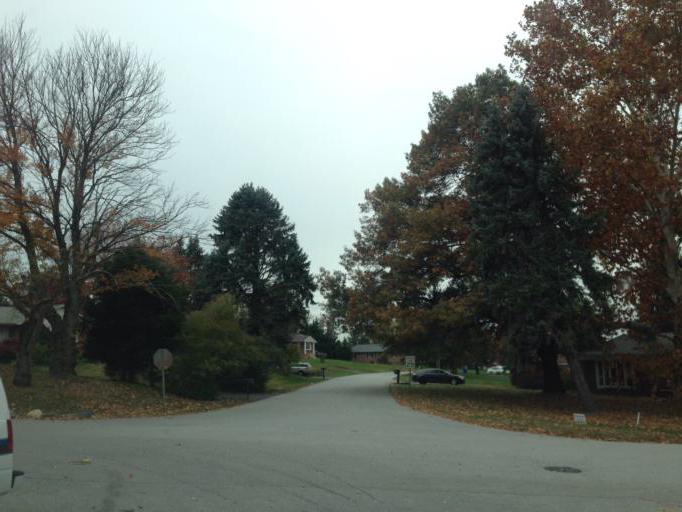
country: US
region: Maryland
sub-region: Howard County
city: Ellicott City
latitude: 39.3037
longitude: -76.8294
